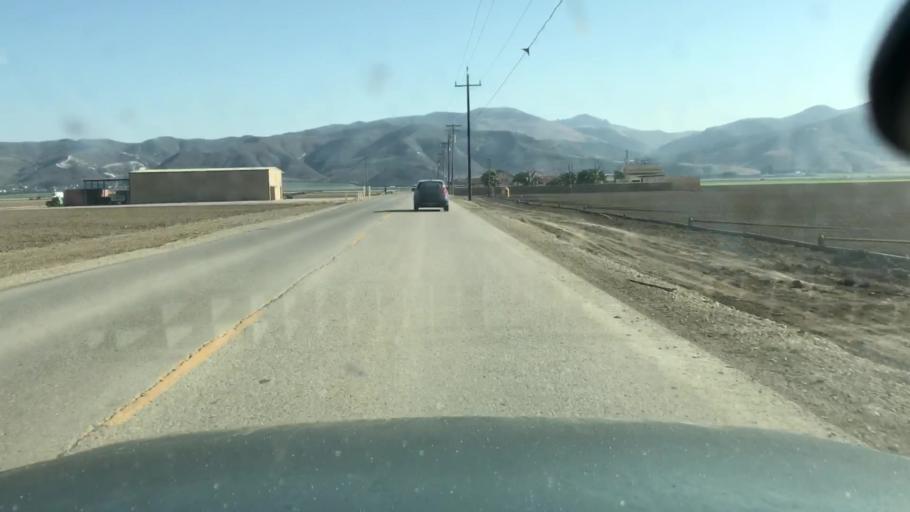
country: US
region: California
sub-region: Santa Barbara County
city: Lompoc
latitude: 34.6563
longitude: -120.4930
